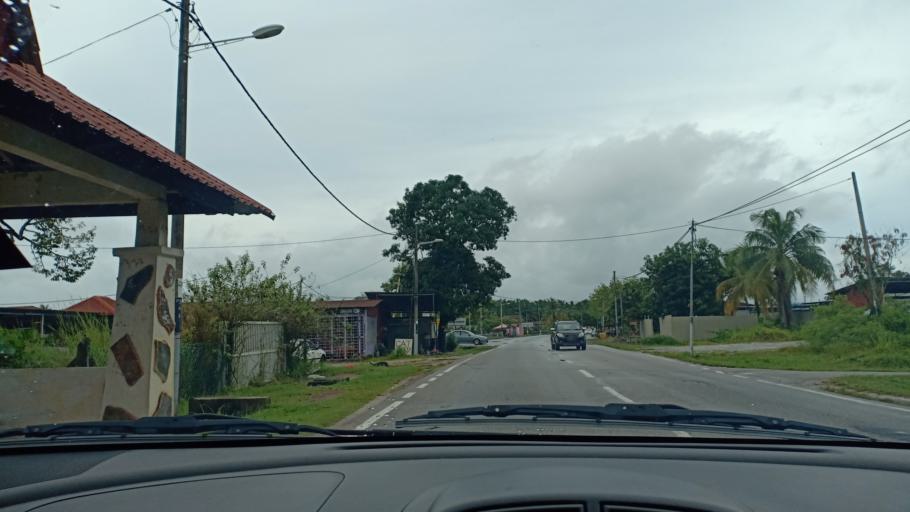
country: MY
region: Penang
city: Kepala Batas
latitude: 5.4945
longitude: 100.4488
